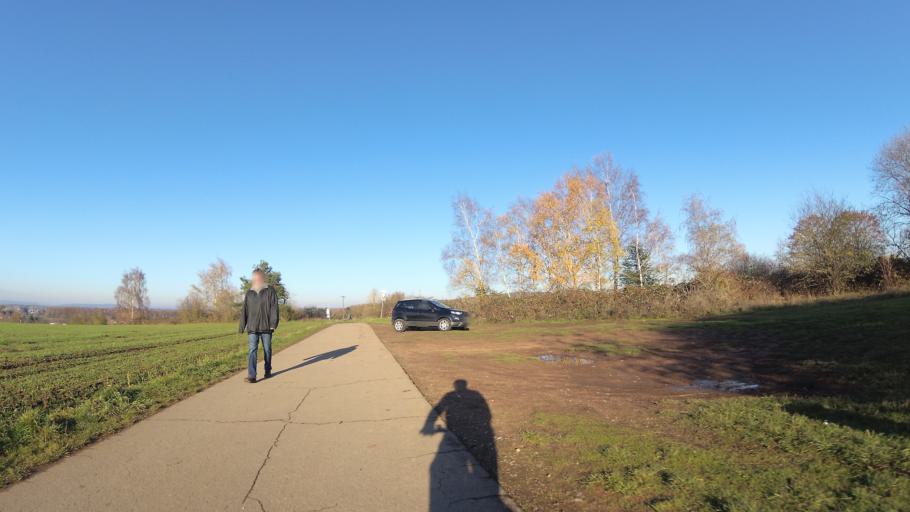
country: DE
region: Saarland
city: Schwalbach
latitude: 49.3019
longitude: 6.8352
